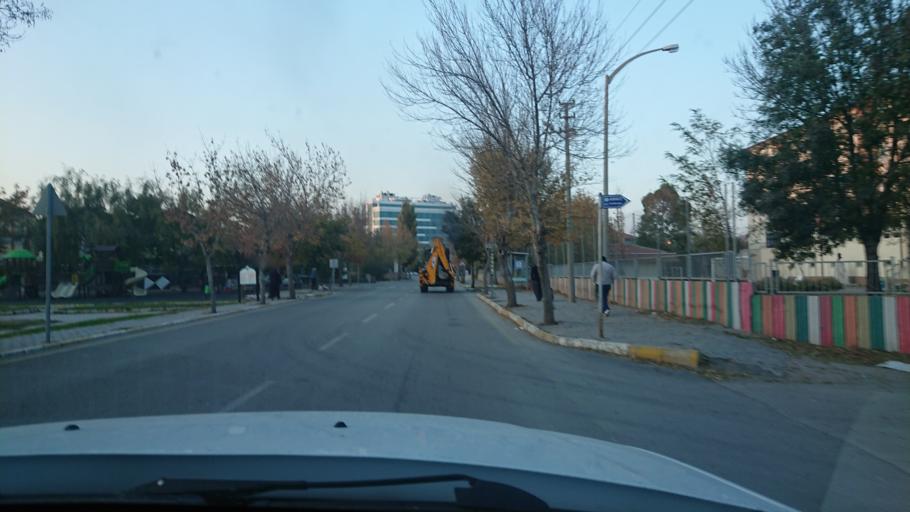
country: TR
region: Aksaray
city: Aksaray
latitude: 38.3563
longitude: 34.0415
